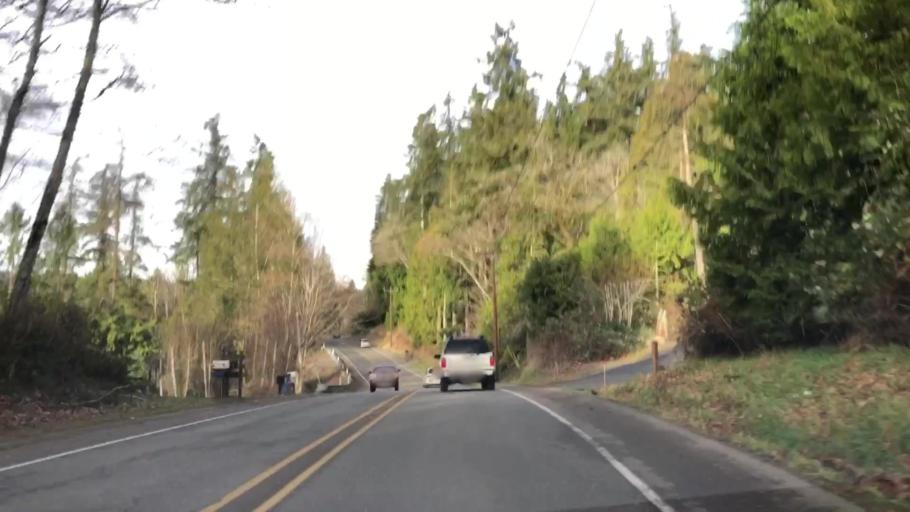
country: US
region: Washington
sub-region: Kitsap County
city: Indianola
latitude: 47.7555
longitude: -122.5486
